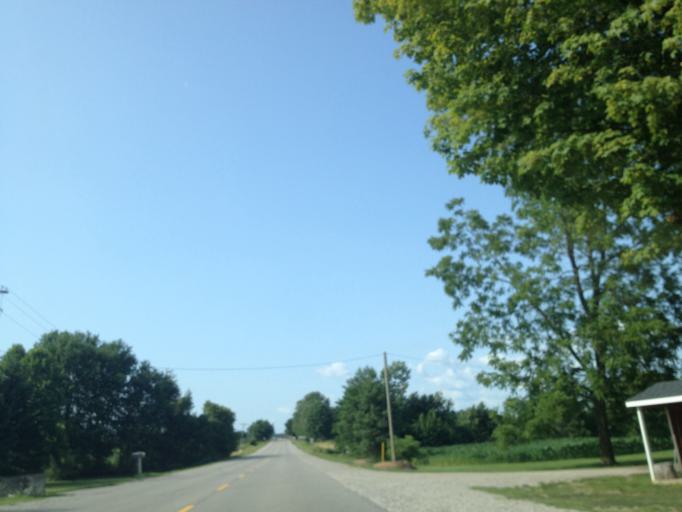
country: CA
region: Ontario
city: Aylmer
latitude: 42.8142
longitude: -80.8322
